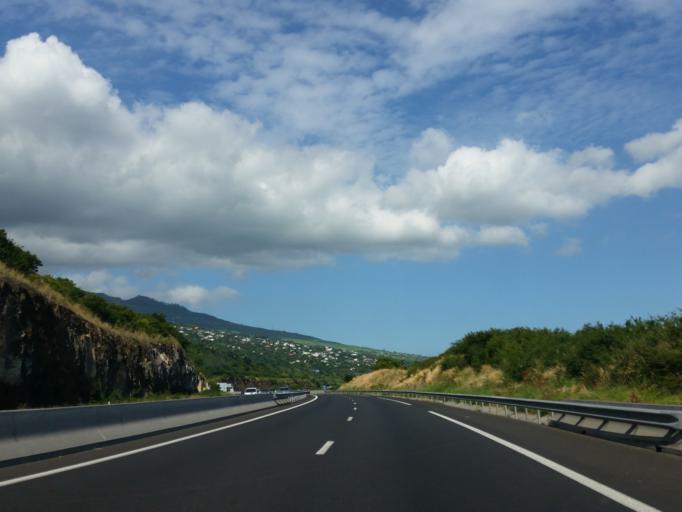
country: RE
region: Reunion
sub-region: Reunion
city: Saint-Leu
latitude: -21.1510
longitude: 55.2908
